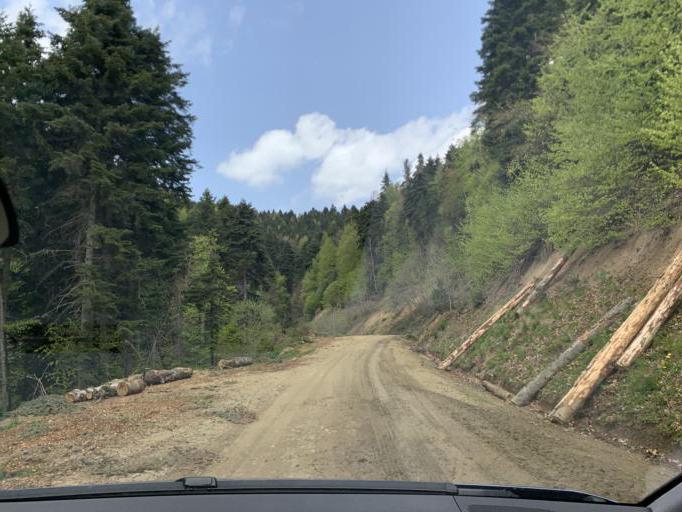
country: TR
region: Bolu
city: Bolu
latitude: 40.8385
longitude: 31.6685
